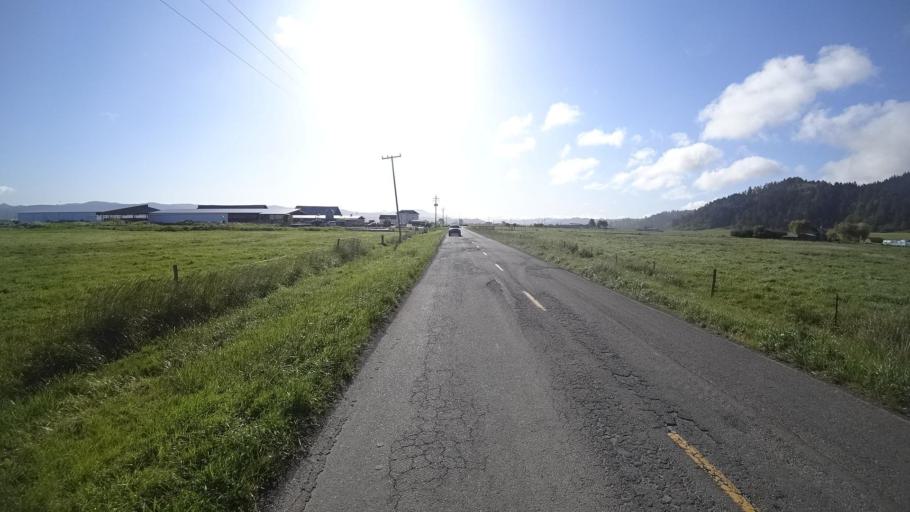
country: US
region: California
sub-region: Humboldt County
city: Ferndale
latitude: 40.5709
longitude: -124.2245
